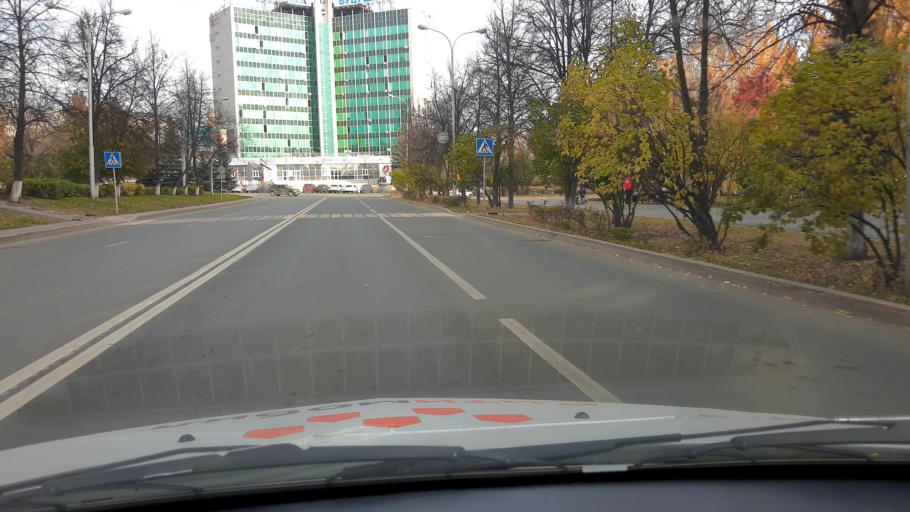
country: RU
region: Bashkortostan
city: Ufa
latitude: 54.8135
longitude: 56.0636
